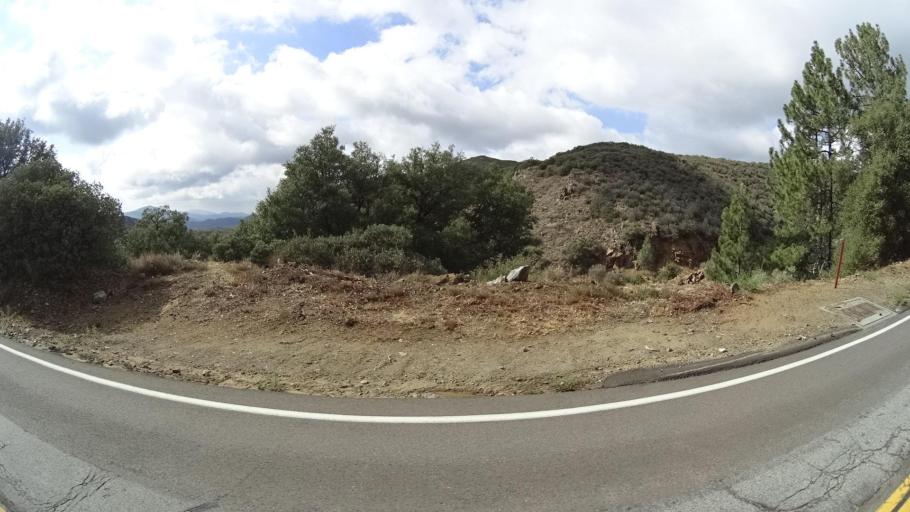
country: US
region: California
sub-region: San Diego County
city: Pine Valley
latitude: 32.8471
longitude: -116.4862
